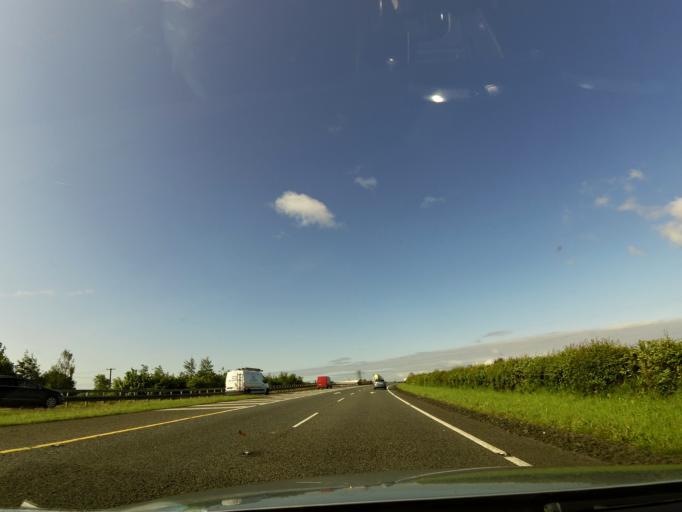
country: IE
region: Munster
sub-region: County Limerick
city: Annacotty
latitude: 52.6455
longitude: -8.5656
